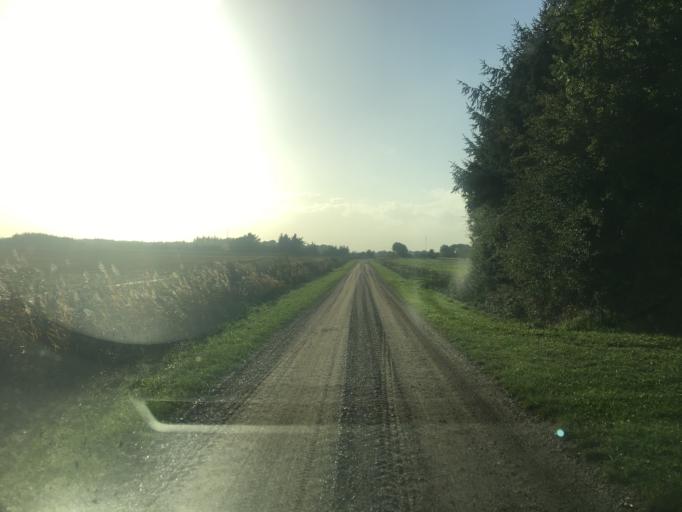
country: DK
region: South Denmark
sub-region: Tonder Kommune
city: Tonder
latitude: 54.9739
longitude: 8.8456
